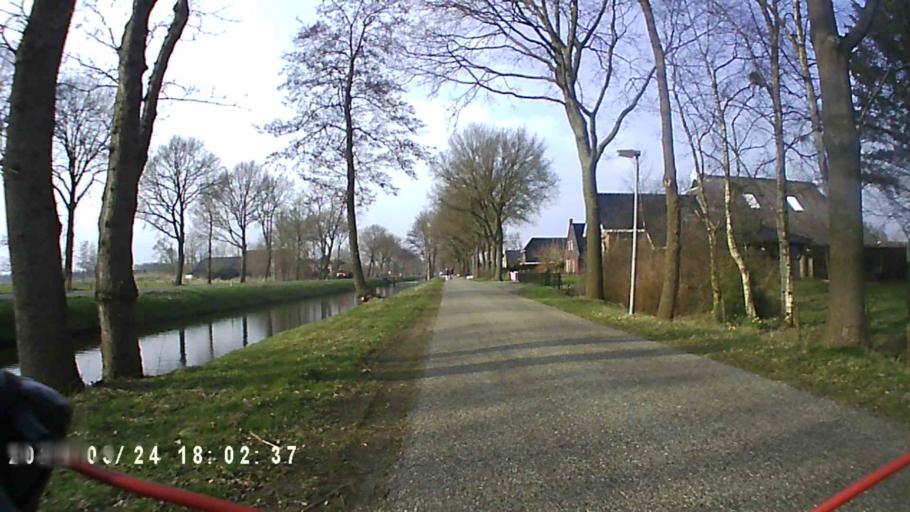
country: NL
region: Groningen
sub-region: Gemeente Leek
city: Leek
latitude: 53.1402
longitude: 6.3601
